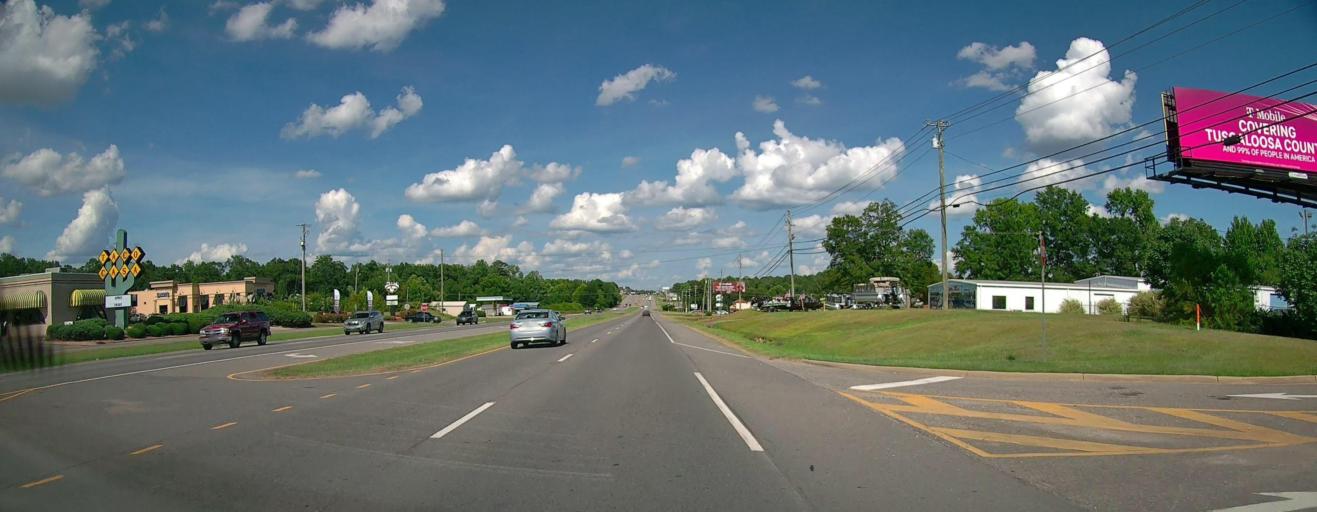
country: US
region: Alabama
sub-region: Tuscaloosa County
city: Northport
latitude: 33.2360
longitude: -87.6090
